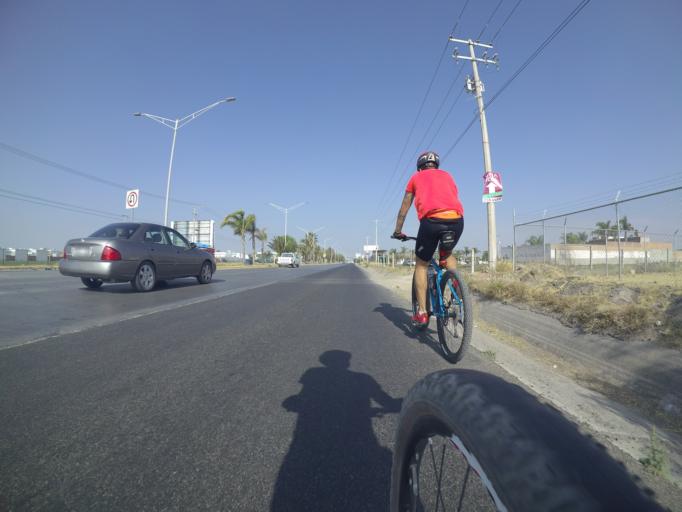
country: MX
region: Aguascalientes
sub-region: Jesus Maria
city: Arboledas Paso Blanco [Fraccionamiento]
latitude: 21.9464
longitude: -102.2997
